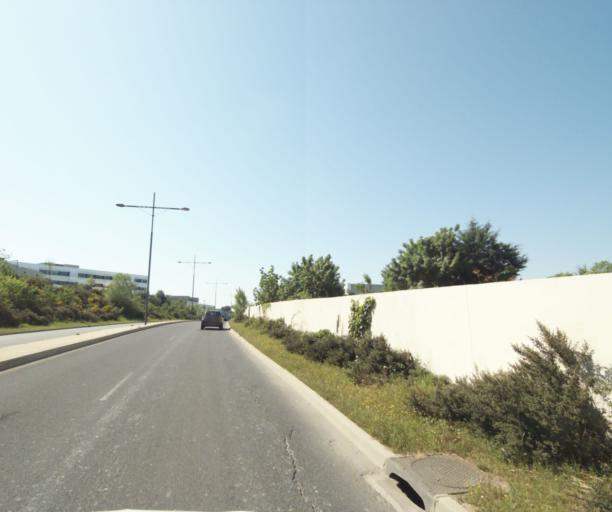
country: FR
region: Languedoc-Roussillon
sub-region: Departement de l'Herault
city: Juvignac
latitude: 43.6213
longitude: 3.8226
